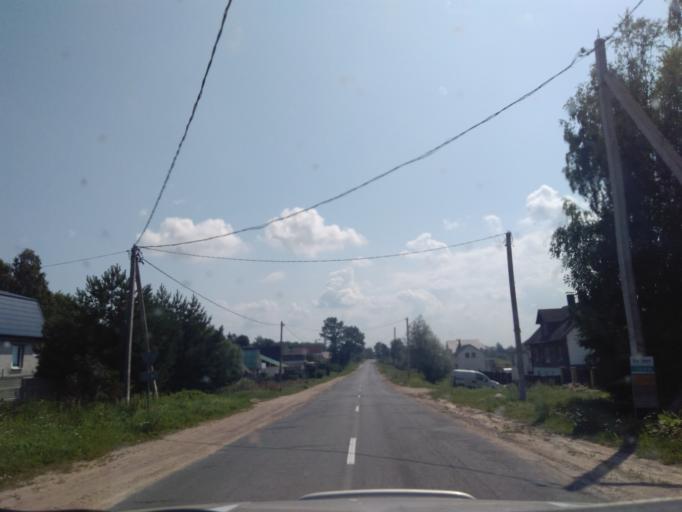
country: BY
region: Minsk
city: Khatsyezhyna
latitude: 53.8927
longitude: 27.2572
